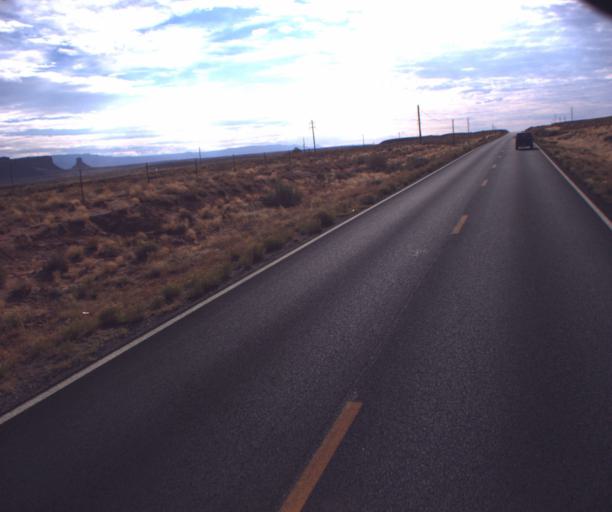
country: US
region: Arizona
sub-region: Apache County
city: Many Farms
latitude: 36.6091
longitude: -109.5757
